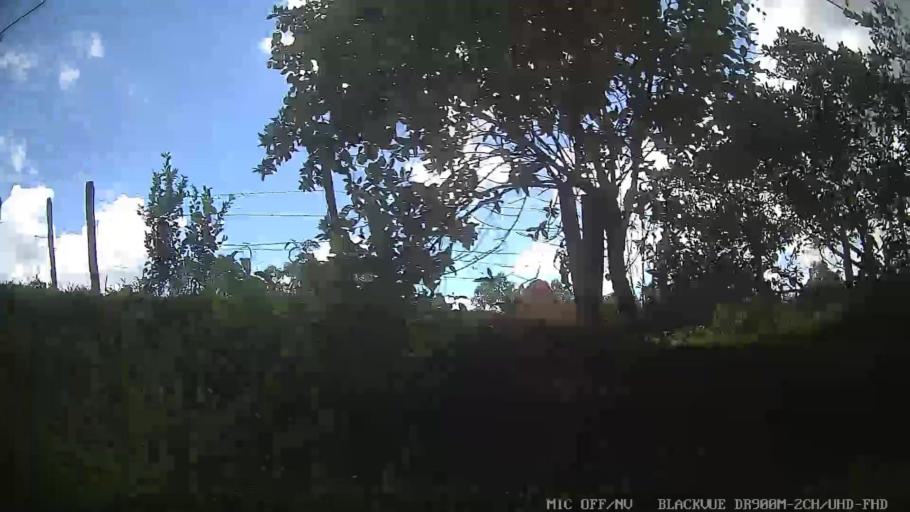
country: BR
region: Sao Paulo
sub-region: Braganca Paulista
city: Braganca Paulista
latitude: -22.9931
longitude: -46.4863
